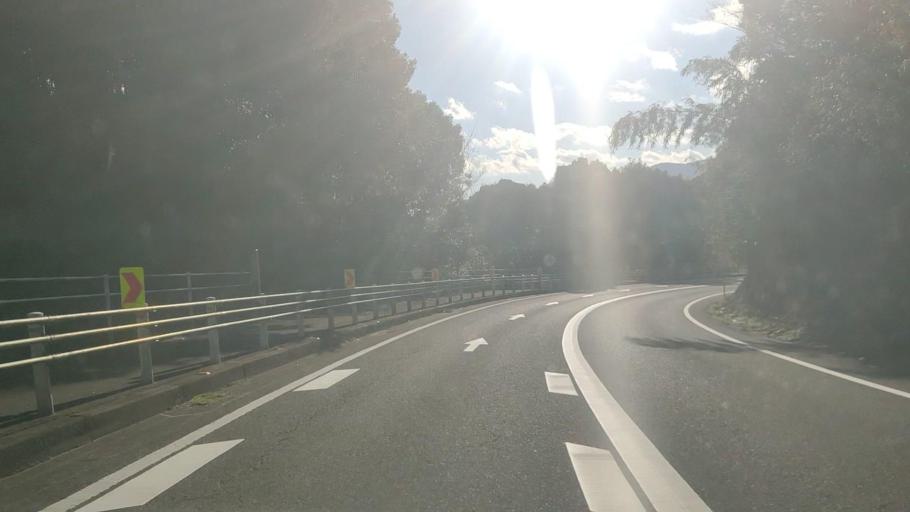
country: JP
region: Saga Prefecture
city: Kanzakimachi-kanzaki
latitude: 33.3814
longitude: 130.2584
